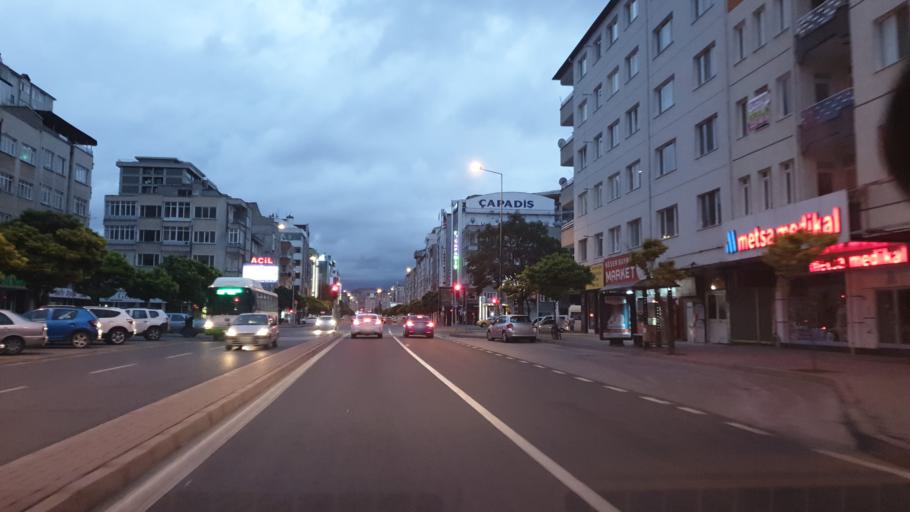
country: TR
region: Kayseri
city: Kayseri
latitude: 38.7259
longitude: 35.4802
